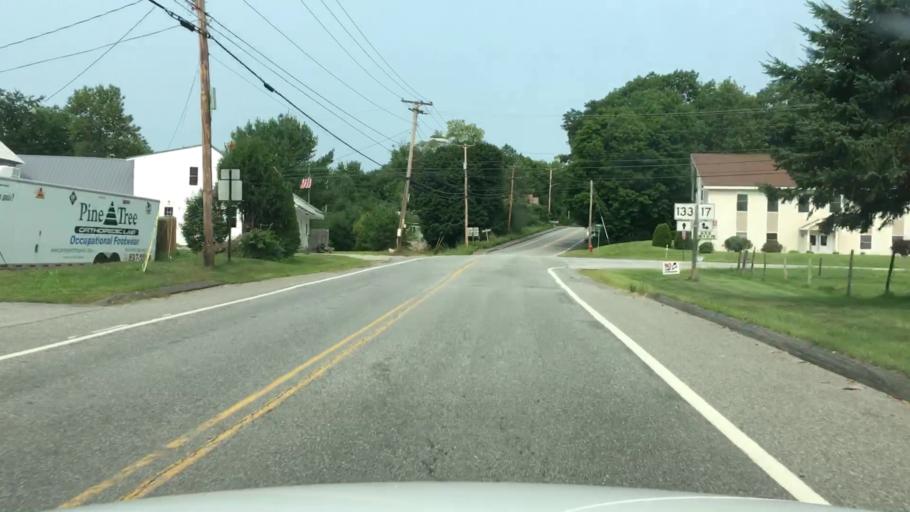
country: US
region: Maine
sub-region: Androscoggin County
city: Livermore Falls
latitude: 44.4625
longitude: -70.1787
